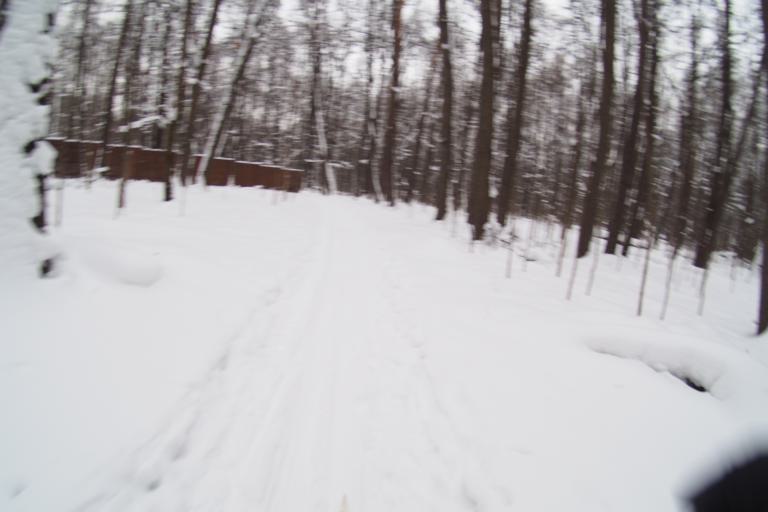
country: RU
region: Moskovskaya
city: Izmaylovo
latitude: 55.7752
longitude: 37.7866
